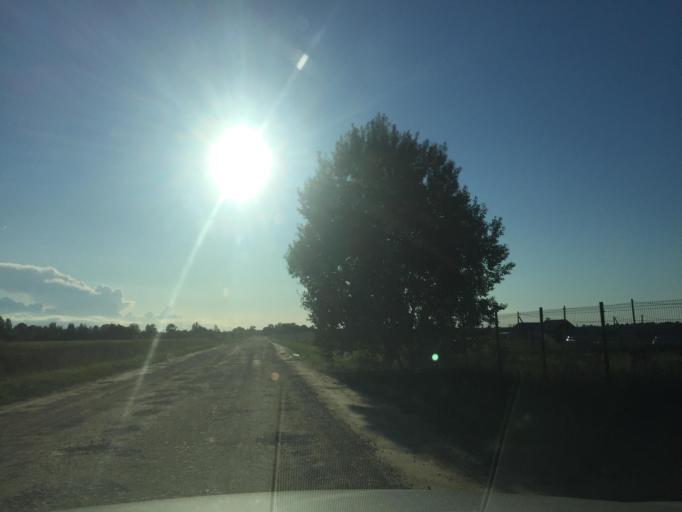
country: RU
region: Leningrad
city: Rozhdestveno
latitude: 59.3327
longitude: 30.0080
